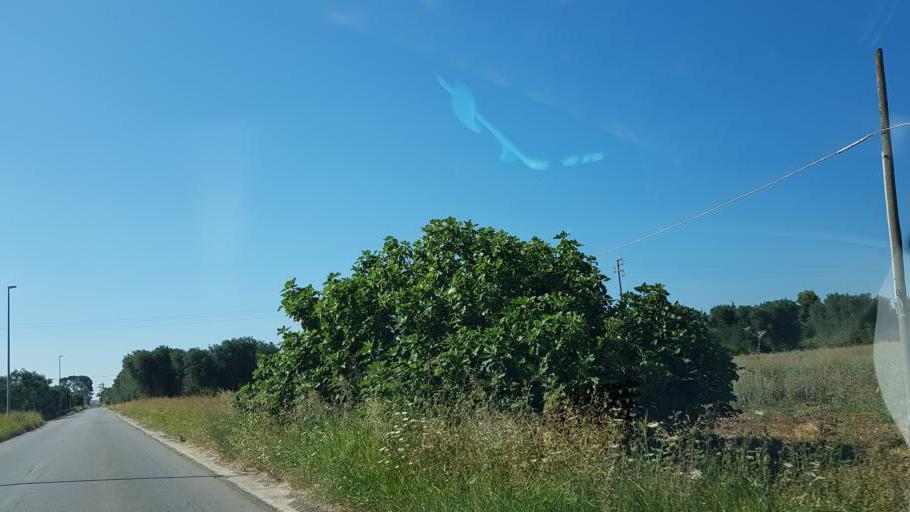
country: IT
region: Apulia
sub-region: Provincia di Brindisi
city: Mesagne
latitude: 40.5463
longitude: 17.8208
